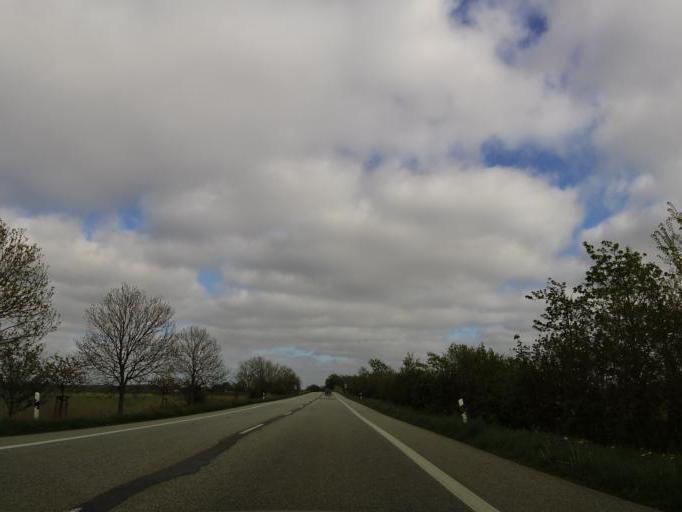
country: DE
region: Schleswig-Holstein
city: Risum-Lindholm
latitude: 54.7552
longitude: 8.8916
